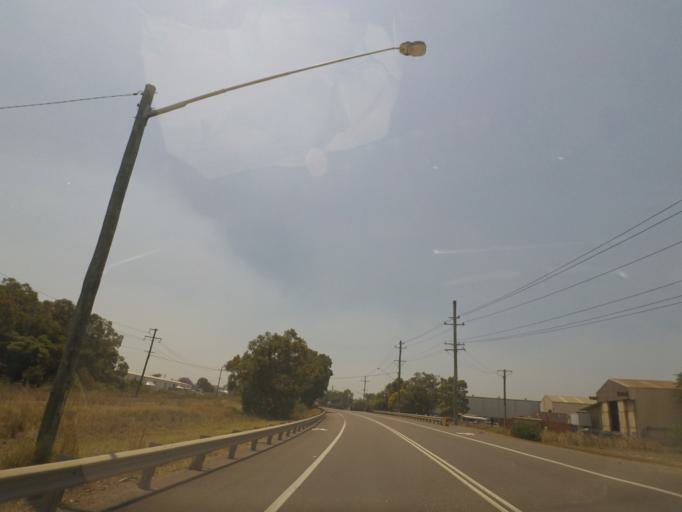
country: AU
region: New South Wales
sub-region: Newcastle
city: Mayfield West
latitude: -32.8328
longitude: 151.7227
